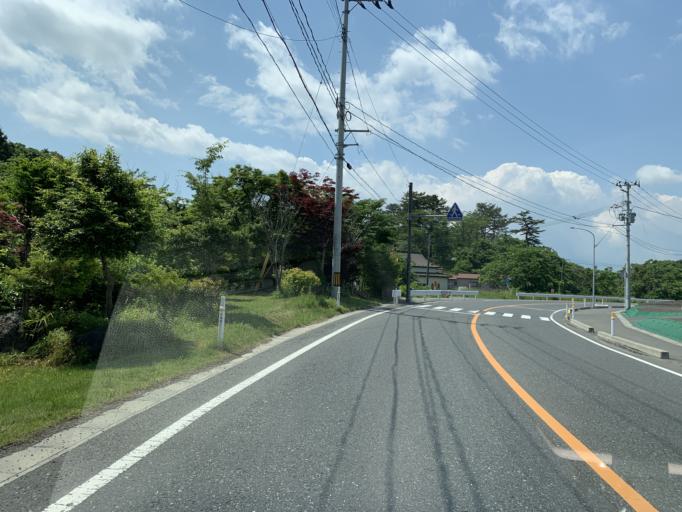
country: JP
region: Miyagi
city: Kogota
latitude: 38.5391
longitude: 141.0572
